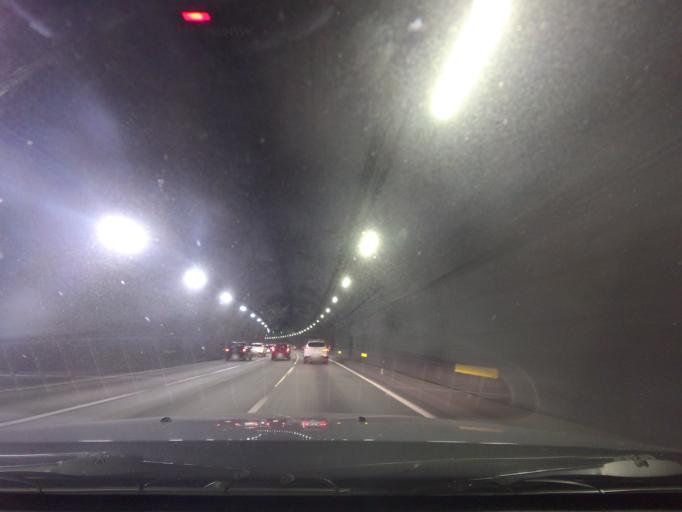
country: BR
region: Sao Paulo
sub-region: Cubatao
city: Cubatao
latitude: -23.8874
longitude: -46.5030
